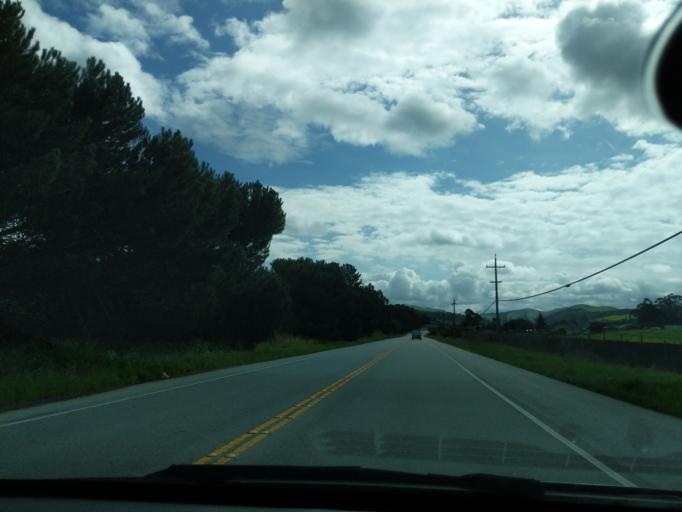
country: US
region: California
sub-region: San Benito County
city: Aromas
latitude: 36.8586
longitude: -121.6486
